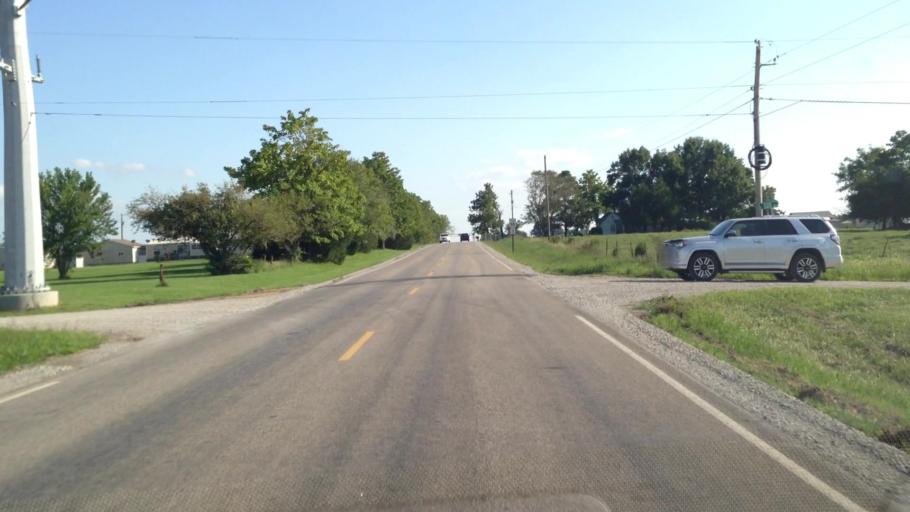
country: US
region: Kansas
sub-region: Crawford County
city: Pittsburg
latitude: 37.3676
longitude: -94.6315
